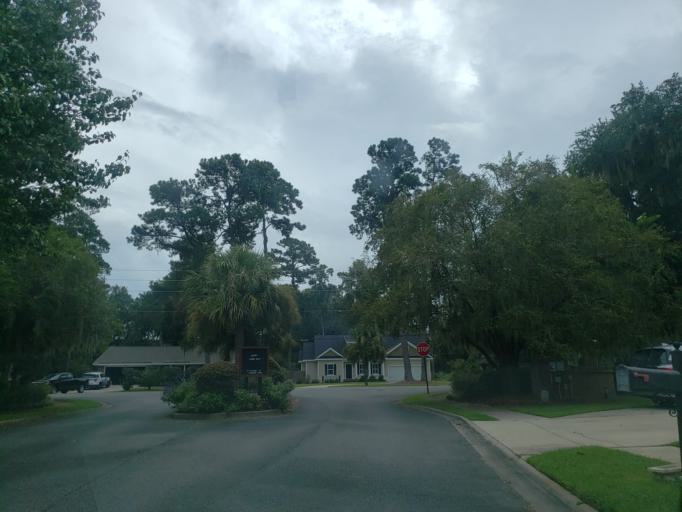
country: US
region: Georgia
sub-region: Chatham County
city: Wilmington Island
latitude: 31.9958
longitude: -80.9763
